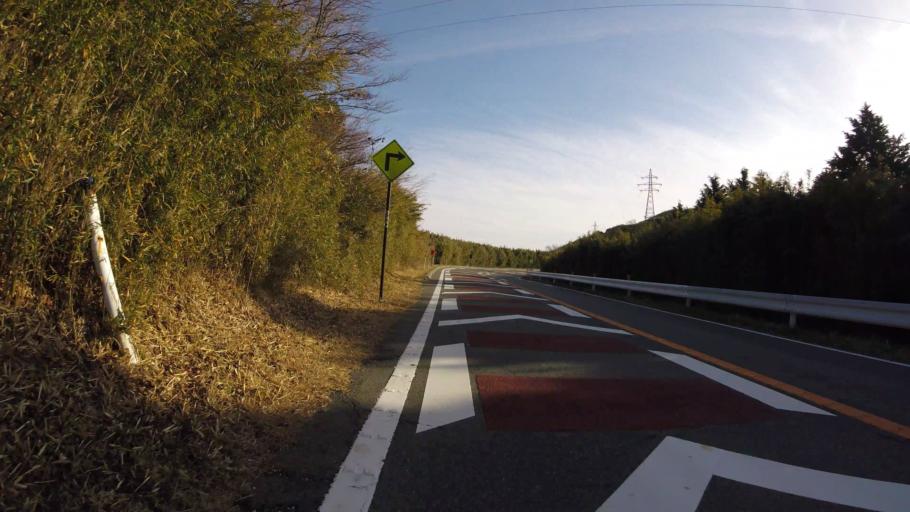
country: JP
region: Kanagawa
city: Yugawara
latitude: 35.1445
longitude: 139.0331
